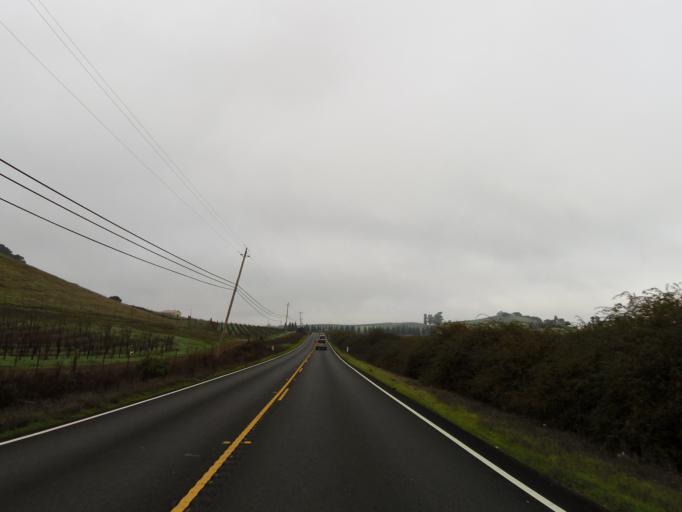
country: US
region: California
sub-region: Sonoma County
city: Temelec
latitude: 38.1959
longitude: -122.4453
